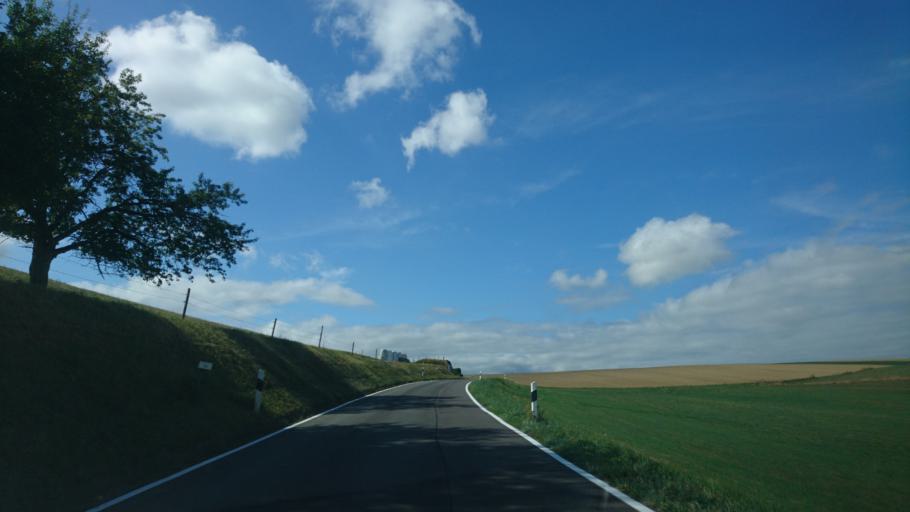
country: DE
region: Rheinland-Pfalz
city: Merzkirchen
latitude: 49.5800
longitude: 6.4851
